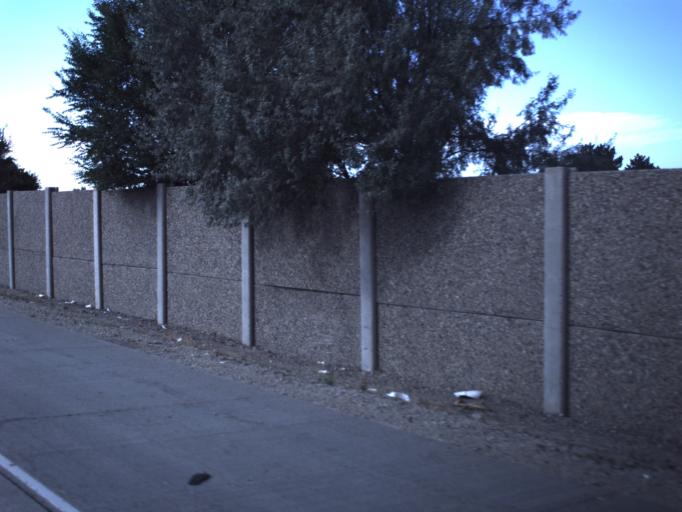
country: US
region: Utah
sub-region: Salt Lake County
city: Taylorsville
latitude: 40.6489
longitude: -111.9505
